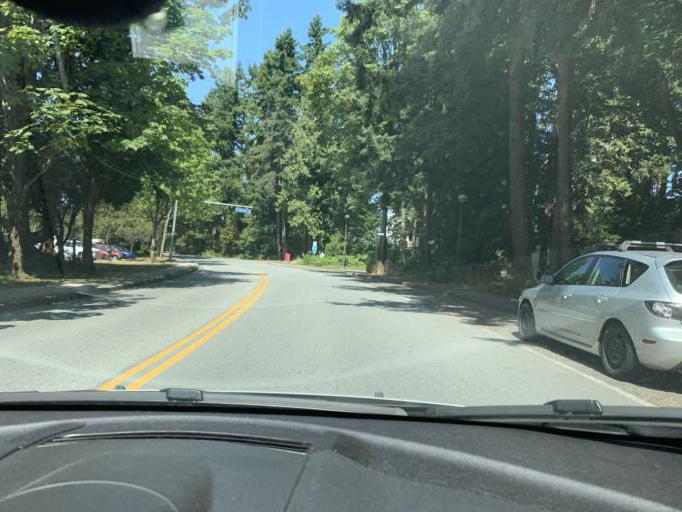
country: CA
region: British Columbia
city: West End
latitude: 49.2593
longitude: -123.2548
